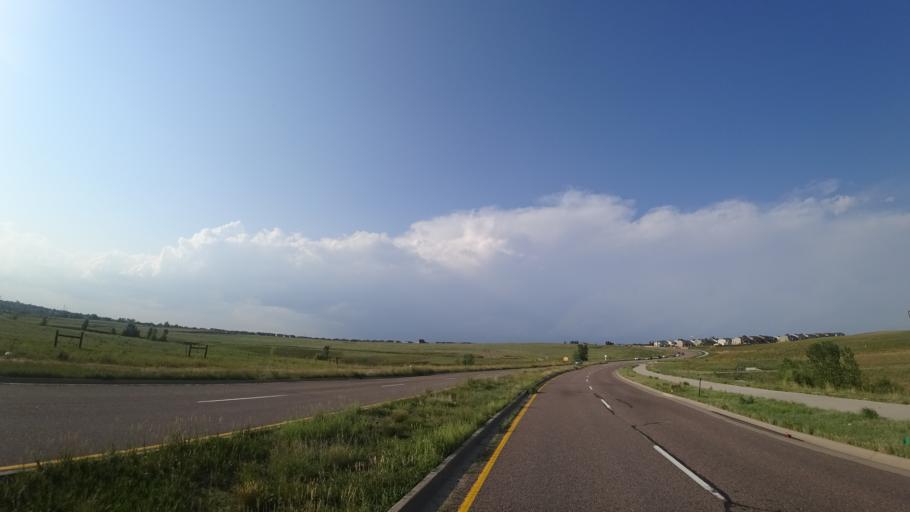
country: US
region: Colorado
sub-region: Arapahoe County
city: Dove Valley
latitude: 39.6323
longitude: -104.7382
